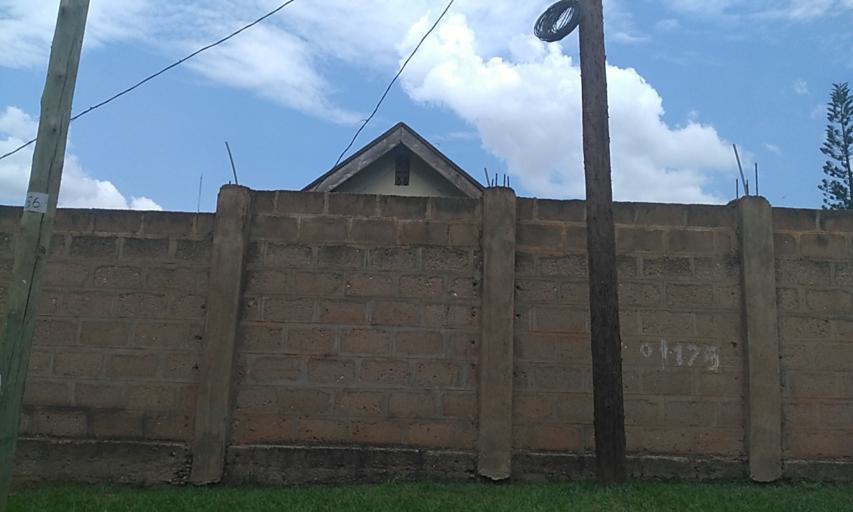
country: UG
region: Central Region
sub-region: Kampala District
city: Kampala
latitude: 0.3366
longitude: 32.6071
